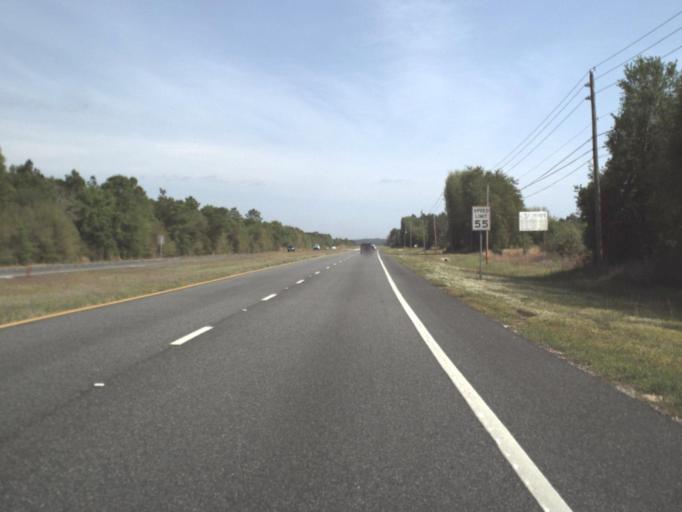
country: US
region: Florida
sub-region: Santa Rosa County
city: East Milton
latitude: 30.6088
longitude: -86.9543
